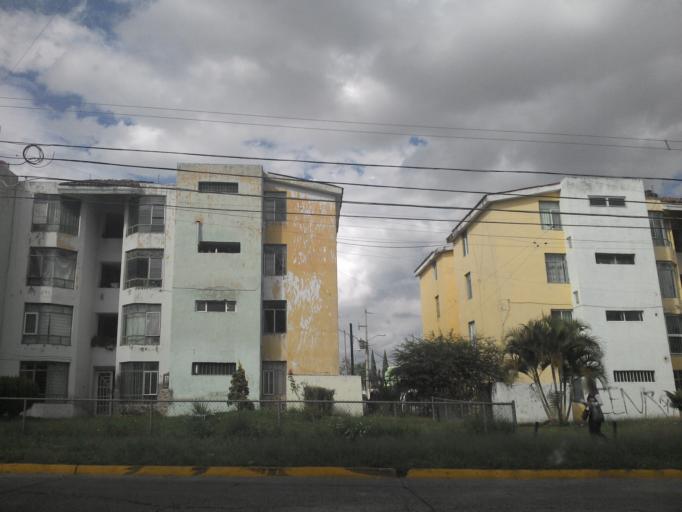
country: MX
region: Jalisco
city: Guadalajara
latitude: 20.6584
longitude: -103.4358
